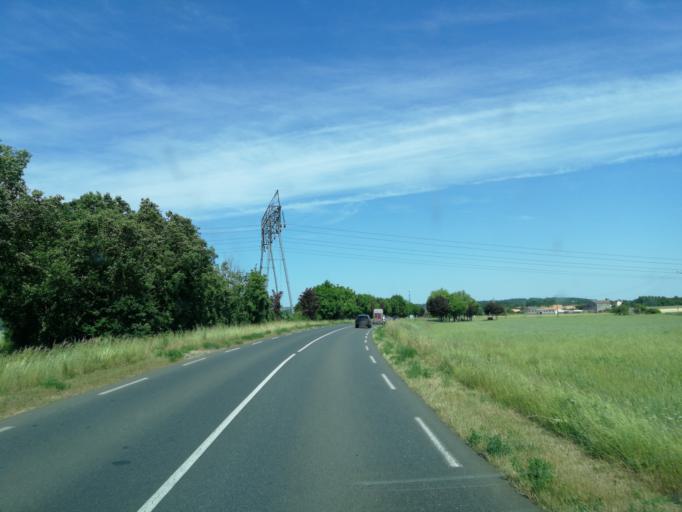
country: FR
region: Poitou-Charentes
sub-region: Departement des Deux-Sevres
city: Saint-Leger-de-Montbrun
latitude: 46.9757
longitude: -0.0618
